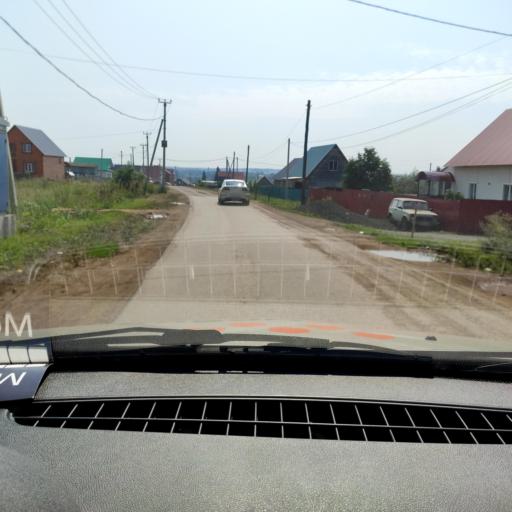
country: RU
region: Bashkortostan
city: Iglino
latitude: 54.8432
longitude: 56.4049
